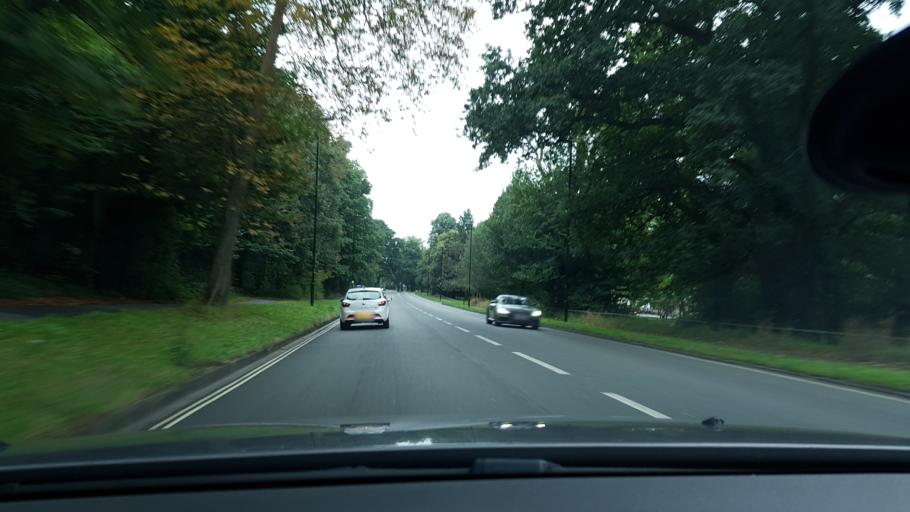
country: GB
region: England
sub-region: Southampton
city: Southampton
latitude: 50.9255
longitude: -1.4054
